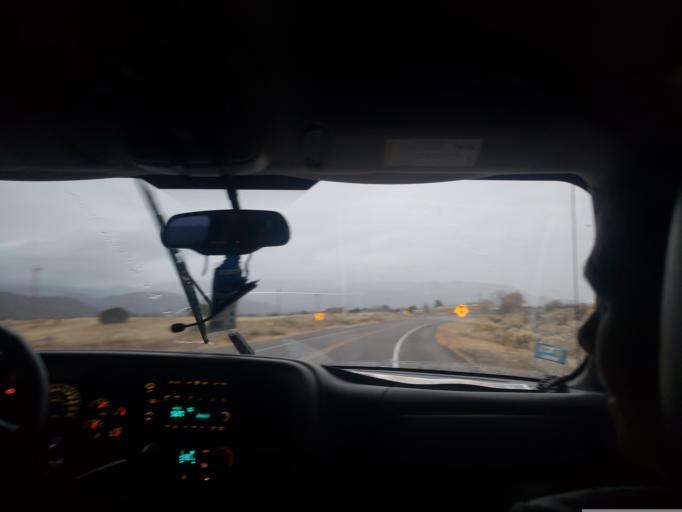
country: US
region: New Mexico
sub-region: Bernalillo County
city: Sandia Heights
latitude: 35.1940
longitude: -106.4974
